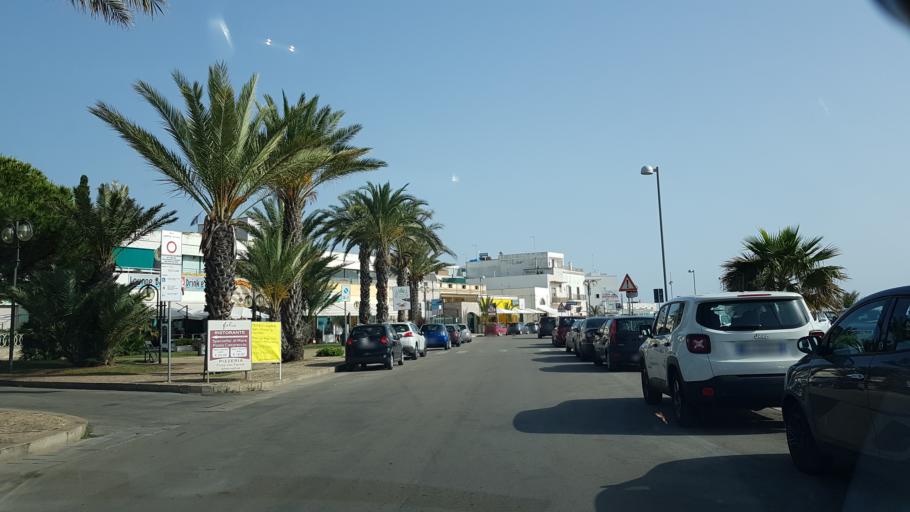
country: IT
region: Apulia
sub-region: Provincia di Lecce
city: Porto Cesareo
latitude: 40.2587
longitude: 17.8911
